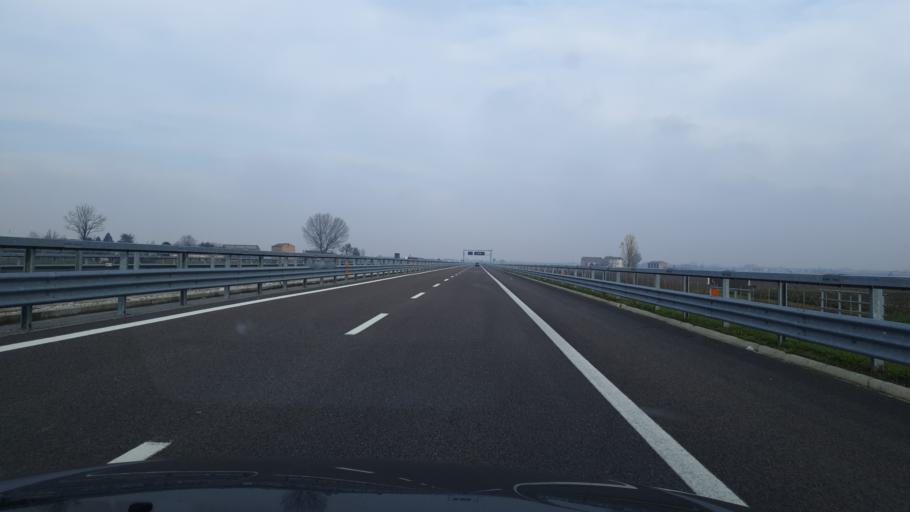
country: IT
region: Veneto
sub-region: Provincia di Padova
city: Saletto
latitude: 45.2448
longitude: 11.5644
